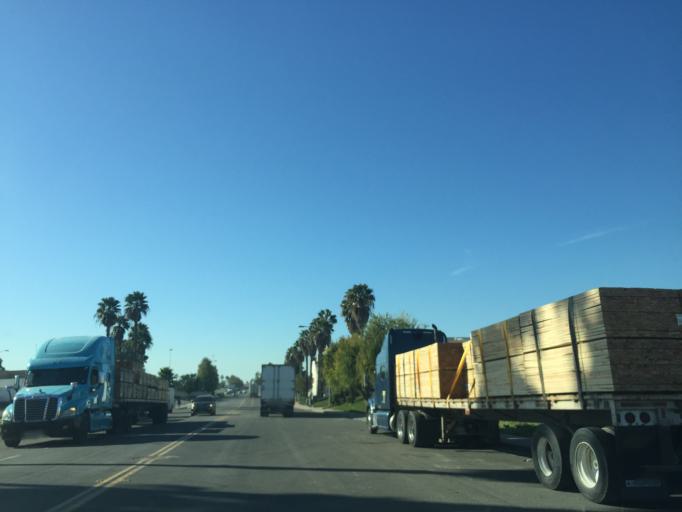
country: MX
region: Baja California
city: Tijuana
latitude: 32.5528
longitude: -116.9285
